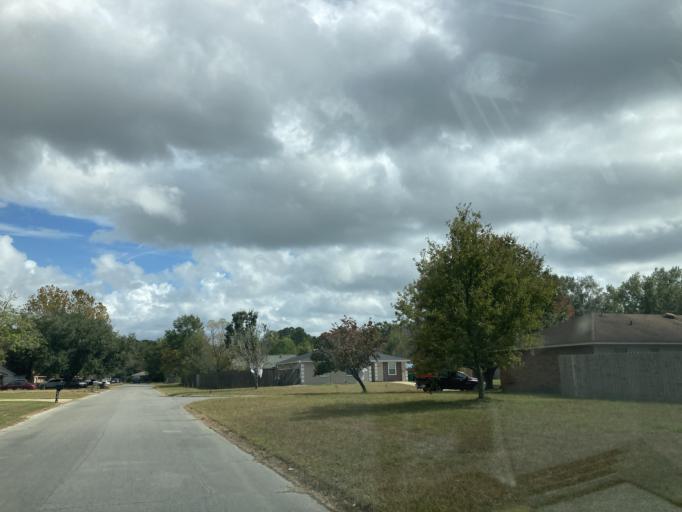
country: US
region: Mississippi
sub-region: Jackson County
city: Gulf Hills
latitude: 30.4461
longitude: -88.8291
